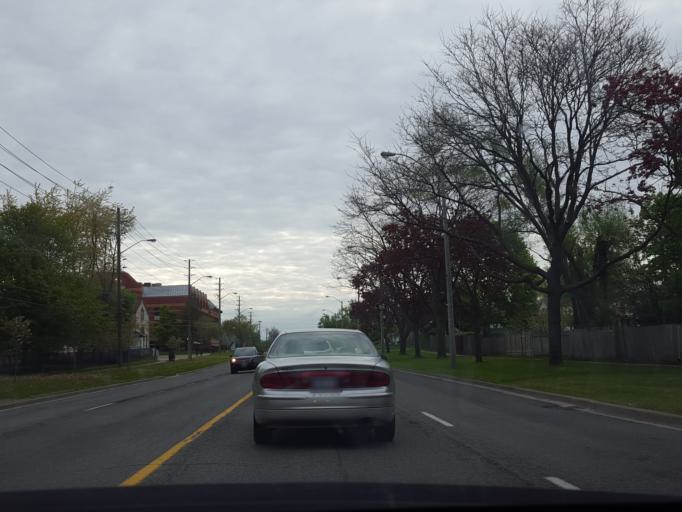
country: CA
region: Ontario
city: Scarborough
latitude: 43.7996
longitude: -79.3031
